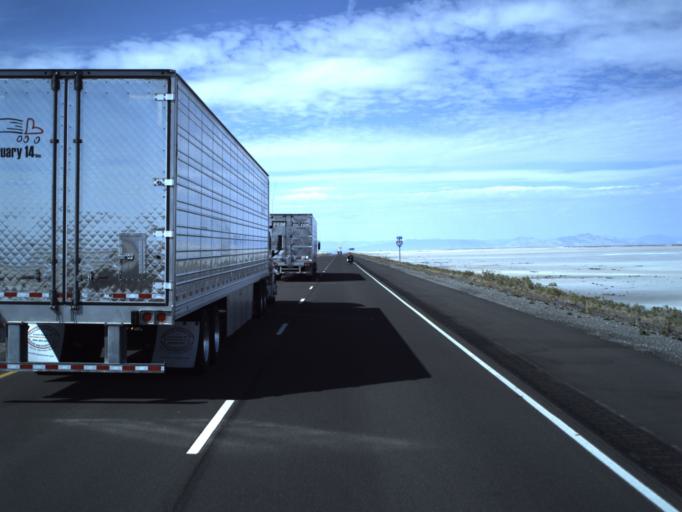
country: US
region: Utah
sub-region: Tooele County
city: Wendover
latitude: 40.7309
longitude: -113.4616
